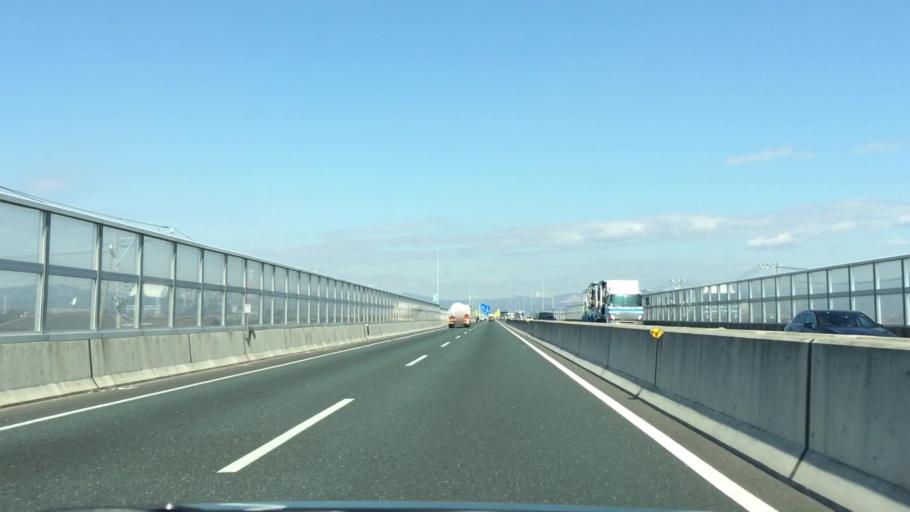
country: JP
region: Aichi
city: Kozakai-cho
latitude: 34.7723
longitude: 137.3324
